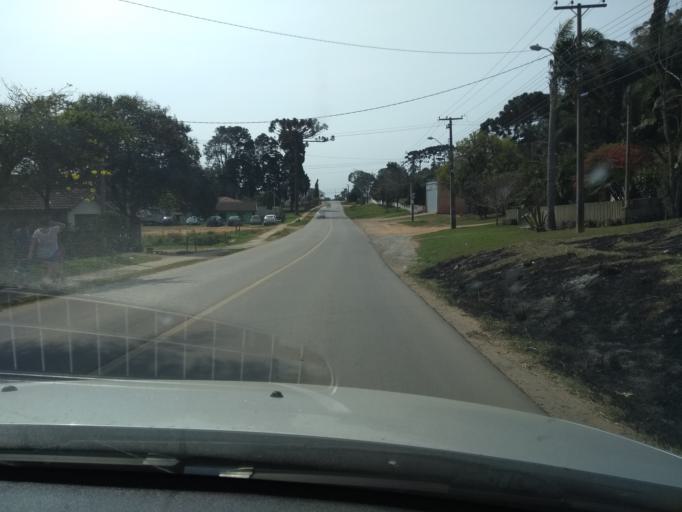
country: BR
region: Parana
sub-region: Araucaria
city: Araucaria
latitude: -25.6166
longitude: -49.3451
